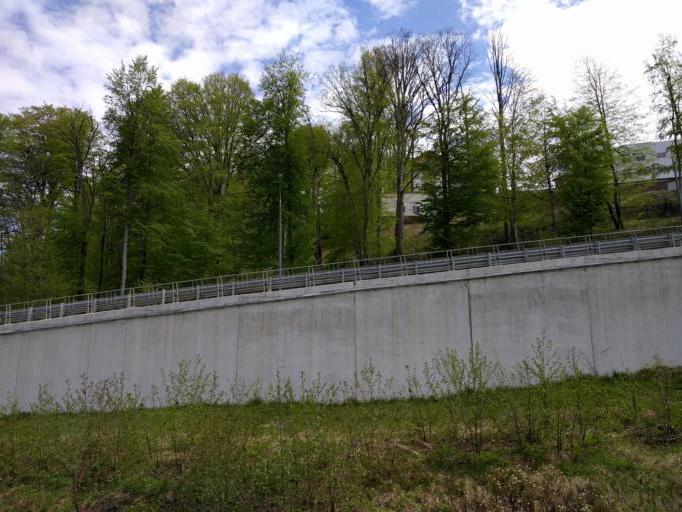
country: RU
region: Krasnodarskiy
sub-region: Sochi City
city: Krasnaya Polyana
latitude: 43.6627
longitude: 40.3126
